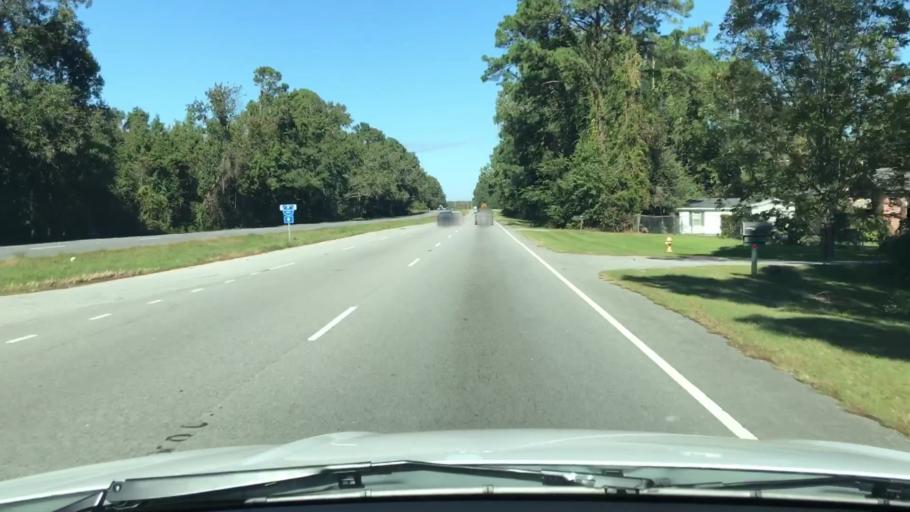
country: US
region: South Carolina
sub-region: Beaufort County
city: Laurel Bay
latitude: 32.5223
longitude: -80.7503
